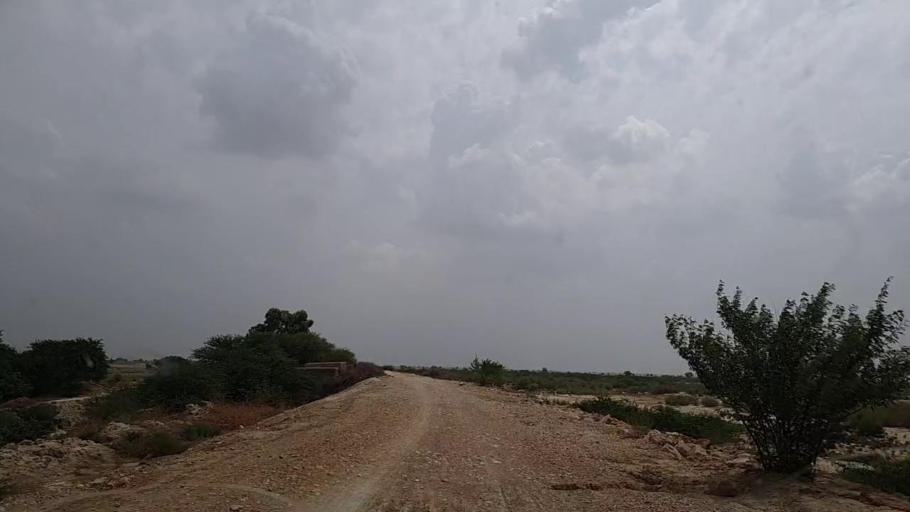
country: PK
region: Sindh
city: Johi
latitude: 26.7330
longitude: 67.5799
